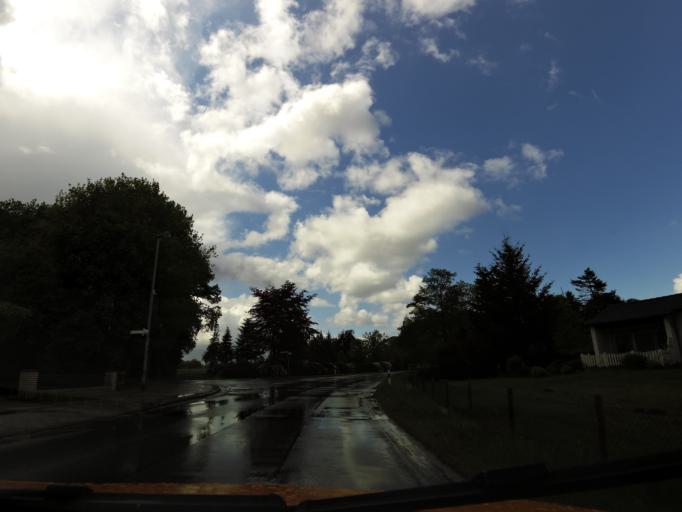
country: DE
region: Lower Saxony
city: Hatten
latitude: 53.1207
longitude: 8.3279
